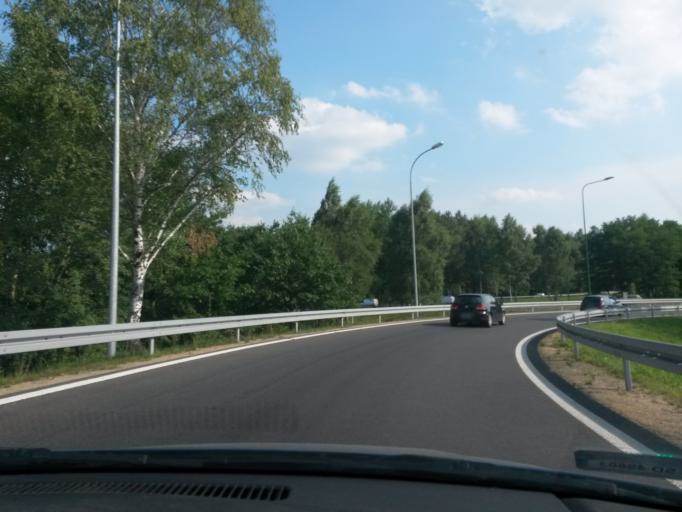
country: PL
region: Silesian Voivodeship
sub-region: Dabrowa Gornicza
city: Dabrowa Gornicza
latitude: 50.3188
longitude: 19.2390
